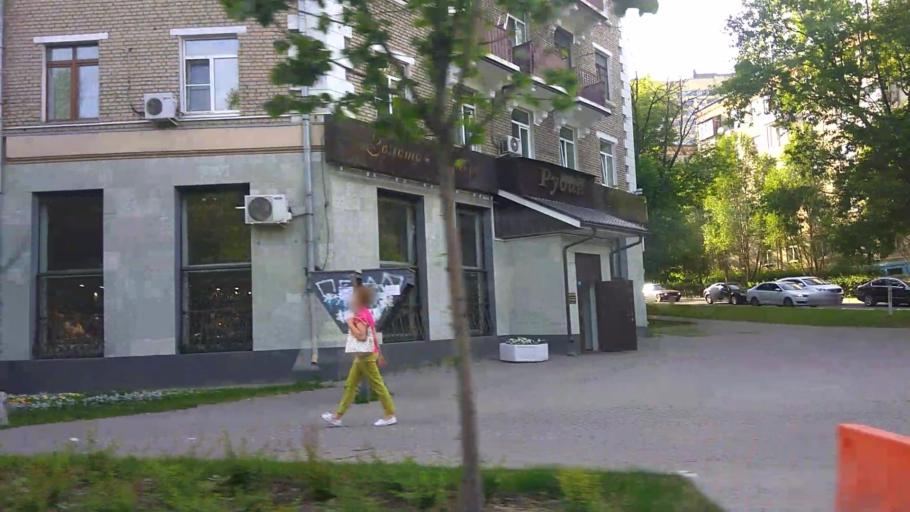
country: RU
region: Moskovskaya
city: Mytishchi
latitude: 55.9134
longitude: 37.7416
